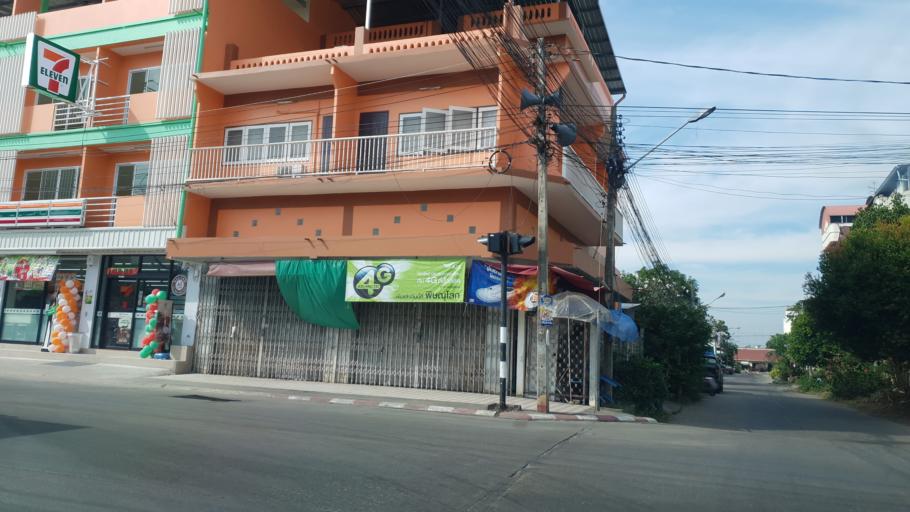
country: TH
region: Phitsanulok
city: Phitsanulok
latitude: 16.8146
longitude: 100.2680
